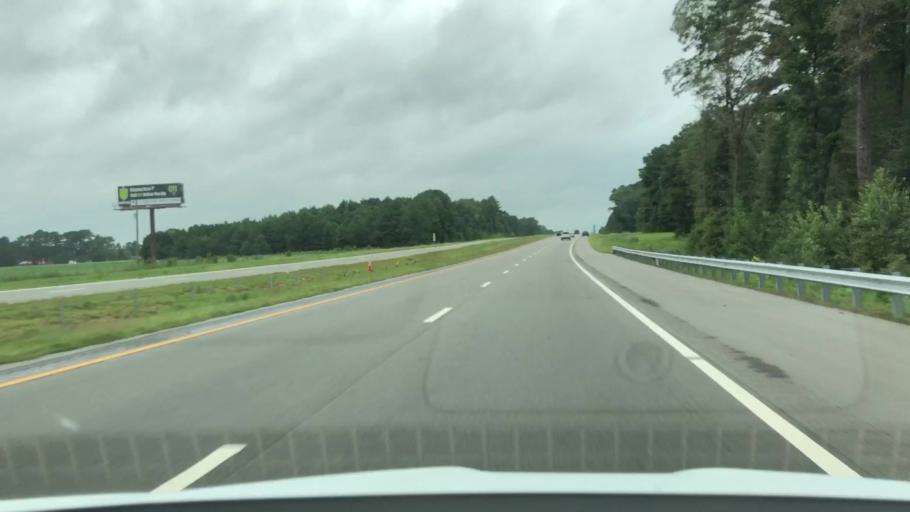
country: US
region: North Carolina
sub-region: Lenoir County
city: La Grange
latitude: 35.3324
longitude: -77.8426
